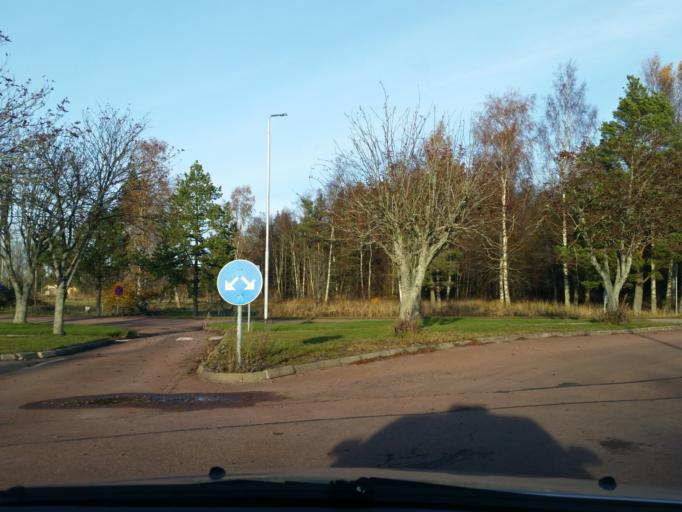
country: AX
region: Mariehamns stad
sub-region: Mariehamn
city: Mariehamn
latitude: 60.1245
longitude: 19.9085
